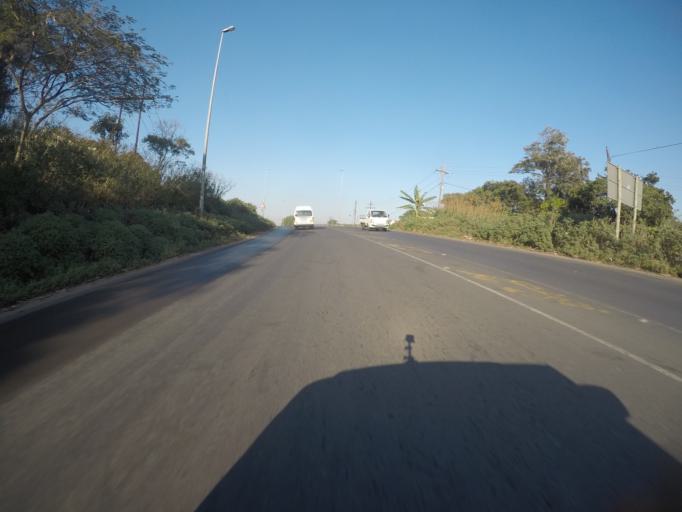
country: ZA
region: KwaZulu-Natal
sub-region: iLembe District Municipality
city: Stanger
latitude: -29.3881
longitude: 31.2513
